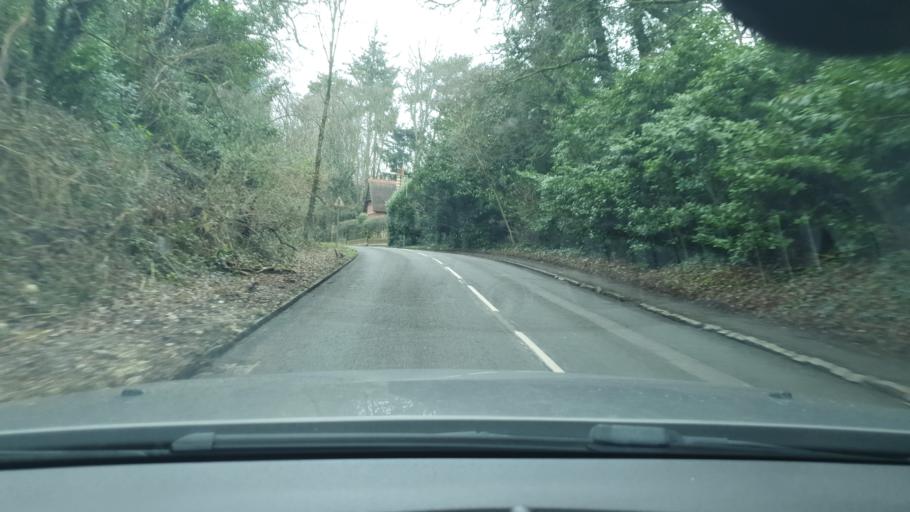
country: GB
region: England
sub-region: Oxfordshire
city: Henley on Thames
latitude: 51.5379
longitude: -0.9132
